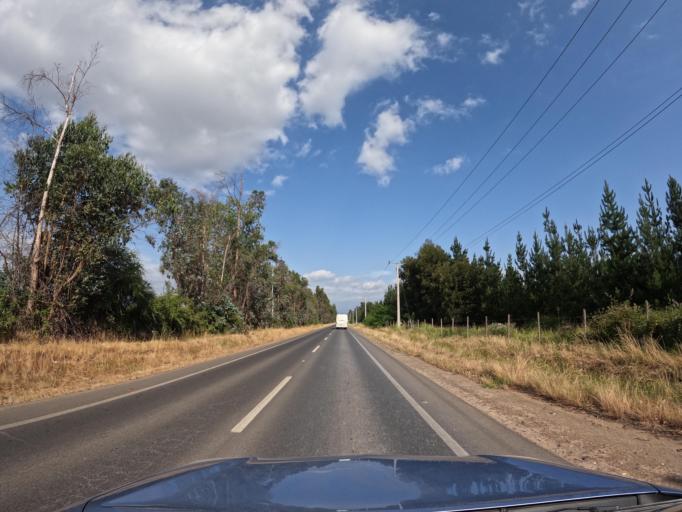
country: CL
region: Maule
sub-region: Provincia de Curico
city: Molina
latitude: -35.2723
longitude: -71.3040
